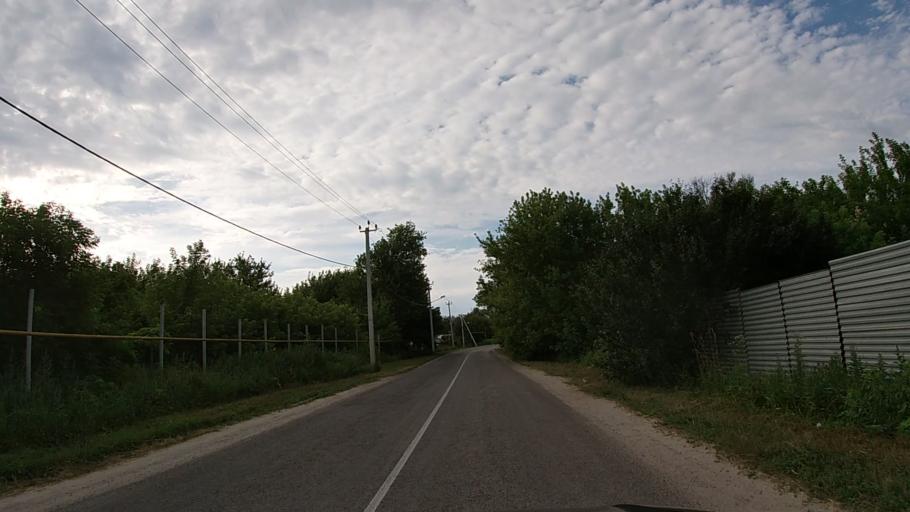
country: RU
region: Belgorod
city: Severnyy
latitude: 50.7087
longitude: 36.5997
